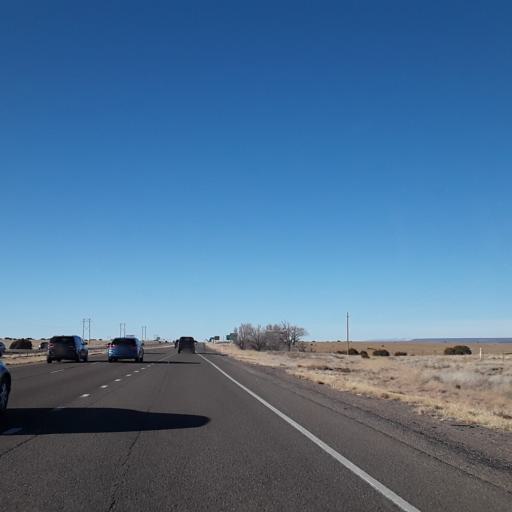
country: US
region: New Mexico
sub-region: Sandoval County
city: Santo Domingo Pueblo
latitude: 35.4692
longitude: -106.3076
